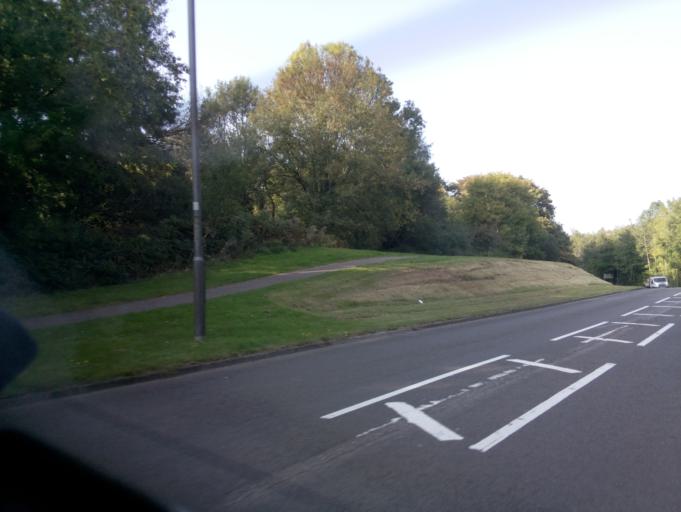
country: GB
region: Wales
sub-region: Torfaen County Borough
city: Cwmbran
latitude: 51.6582
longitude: -3.0451
